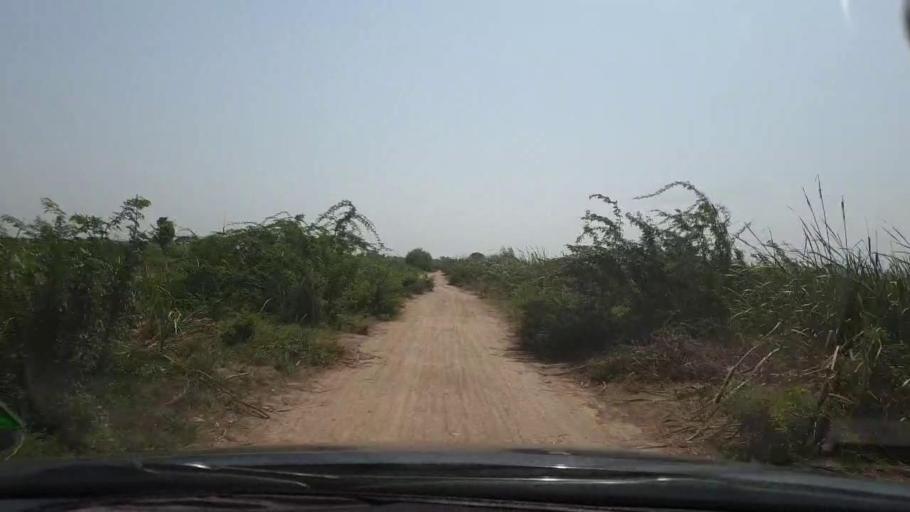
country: PK
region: Sindh
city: Tando Bago
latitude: 24.7891
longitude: 69.1175
